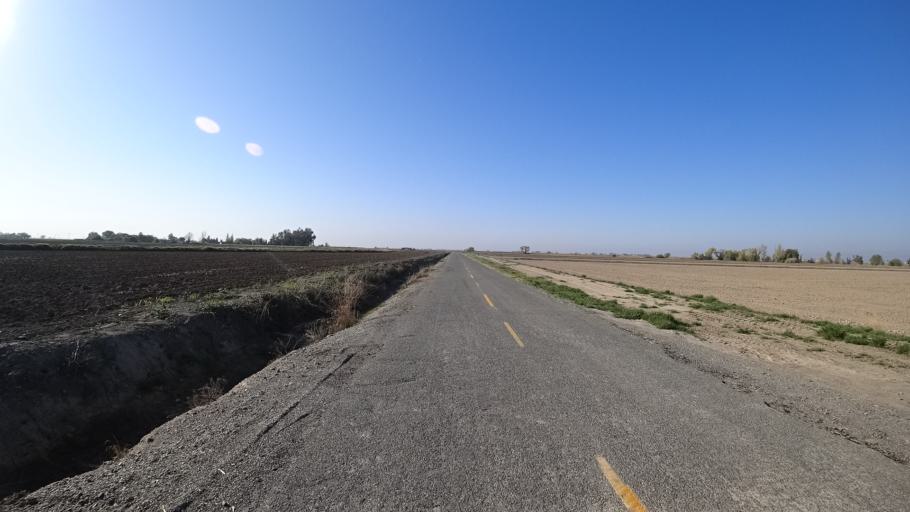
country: US
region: California
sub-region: Glenn County
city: Willows
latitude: 39.5280
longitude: -122.1217
